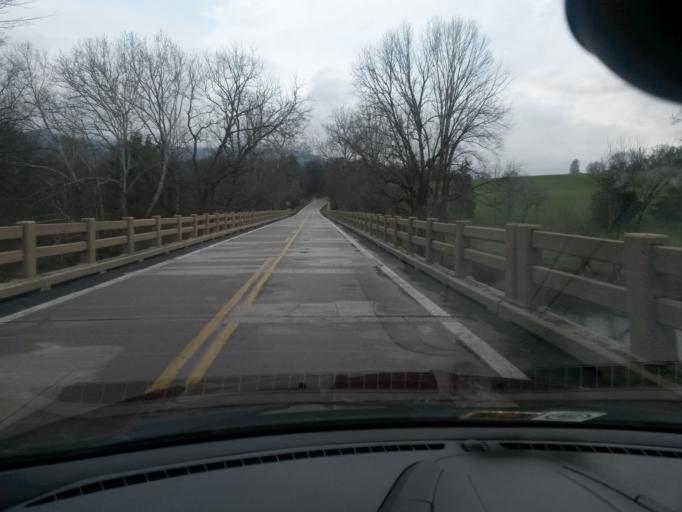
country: US
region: Virginia
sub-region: Alleghany County
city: Clifton Forge
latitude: 37.8903
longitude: -79.7515
